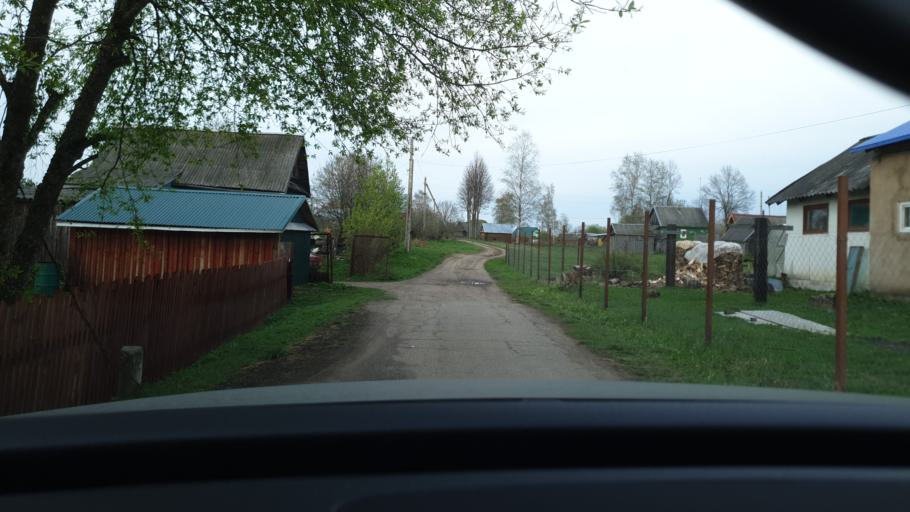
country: RU
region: Tverskaya
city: Berezayka
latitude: 58.0464
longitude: 33.7782
